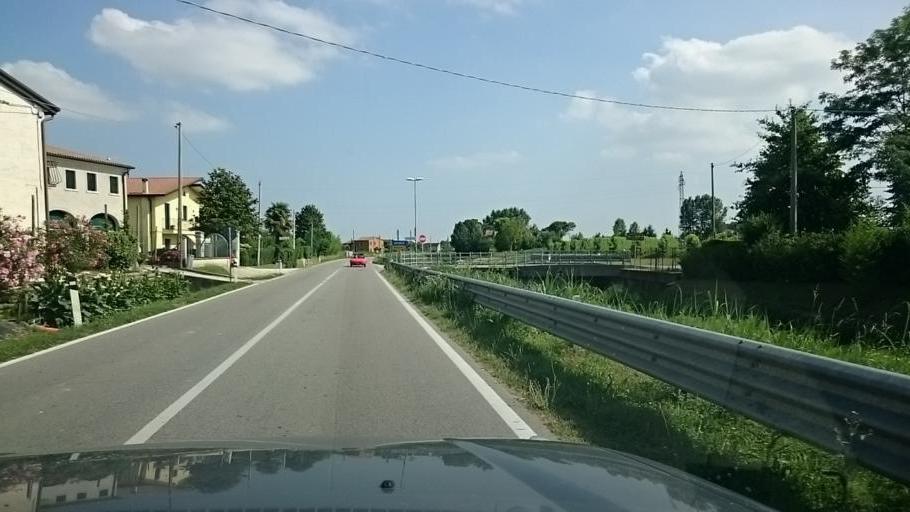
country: IT
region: Veneto
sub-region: Provincia di Padova
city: Villa del Conte
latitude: 45.5594
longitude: 11.8694
